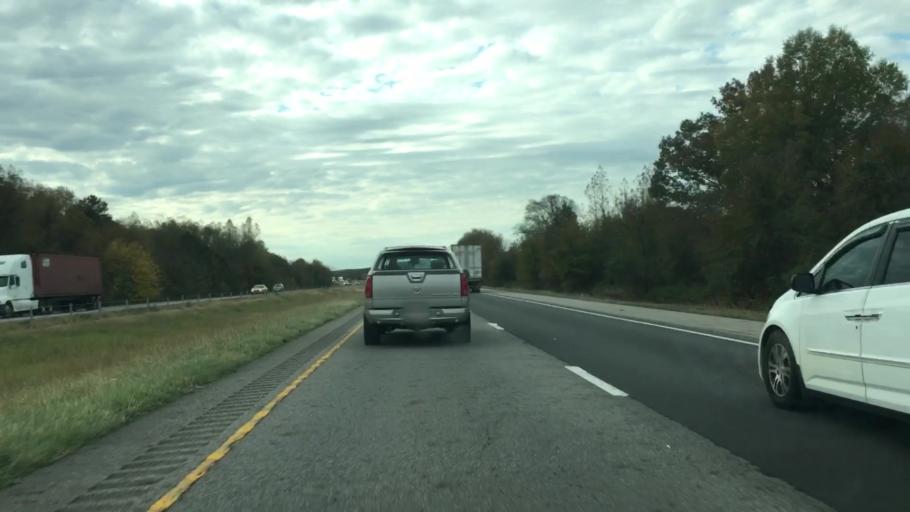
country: US
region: Arkansas
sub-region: Conway County
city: Morrilton
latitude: 35.1629
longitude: -92.6171
